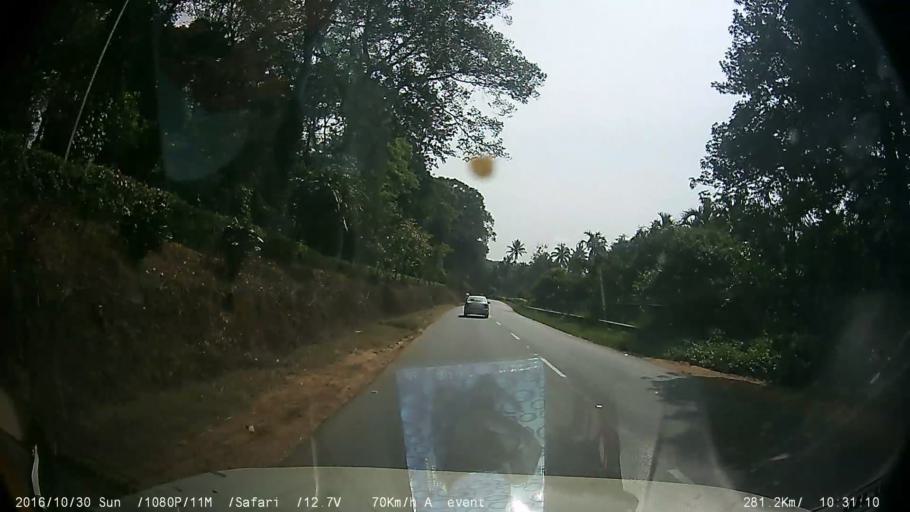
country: IN
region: Karnataka
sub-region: Kodagu
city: Suntikoppa
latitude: 12.4469
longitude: 75.8172
